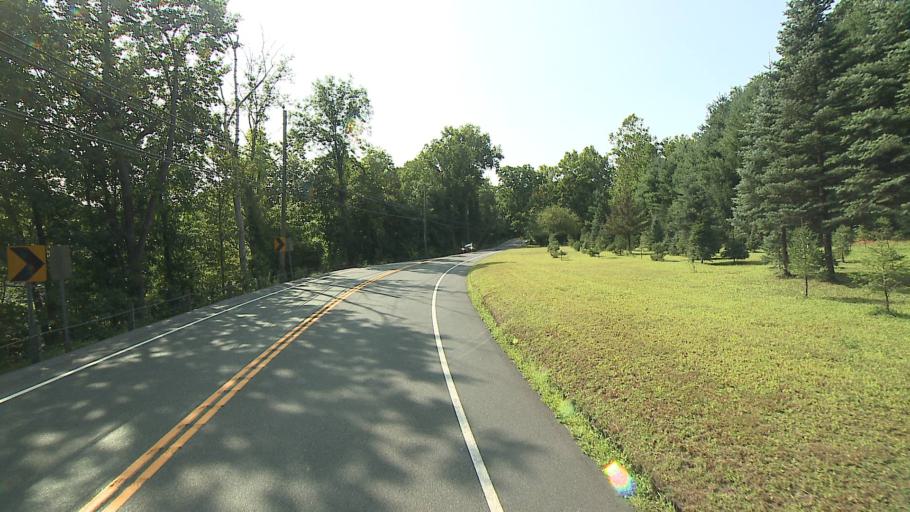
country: US
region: Connecticut
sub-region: Fairfield County
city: Sherman
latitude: 41.6127
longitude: -73.4517
